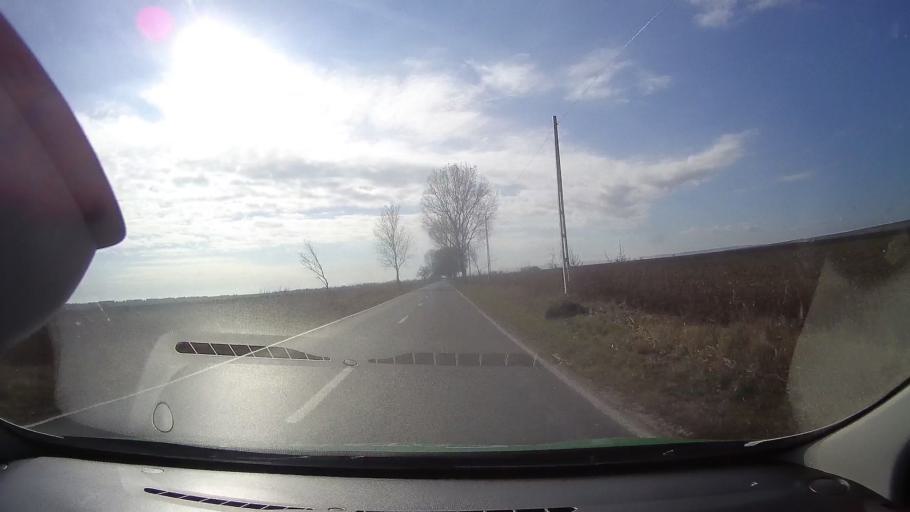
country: RO
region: Tulcea
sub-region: Comuna Valea Nucarilor
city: Agighiol
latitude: 44.9934
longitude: 28.8860
